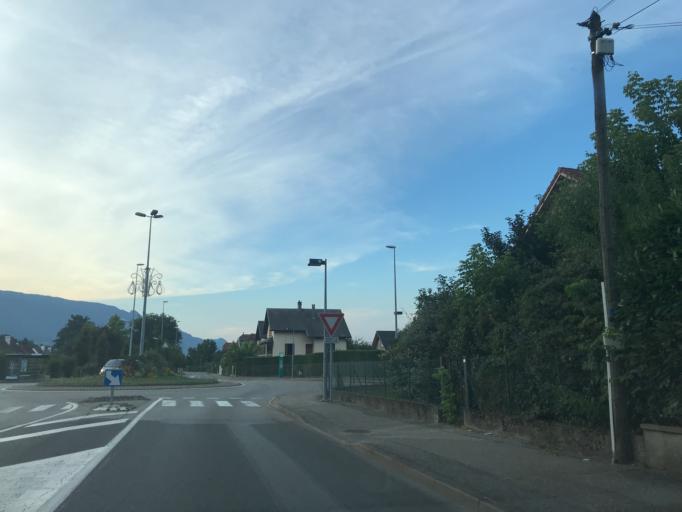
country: FR
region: Rhone-Alpes
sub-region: Departement de la Savoie
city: Cognin
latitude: 45.5683
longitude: 5.8925
